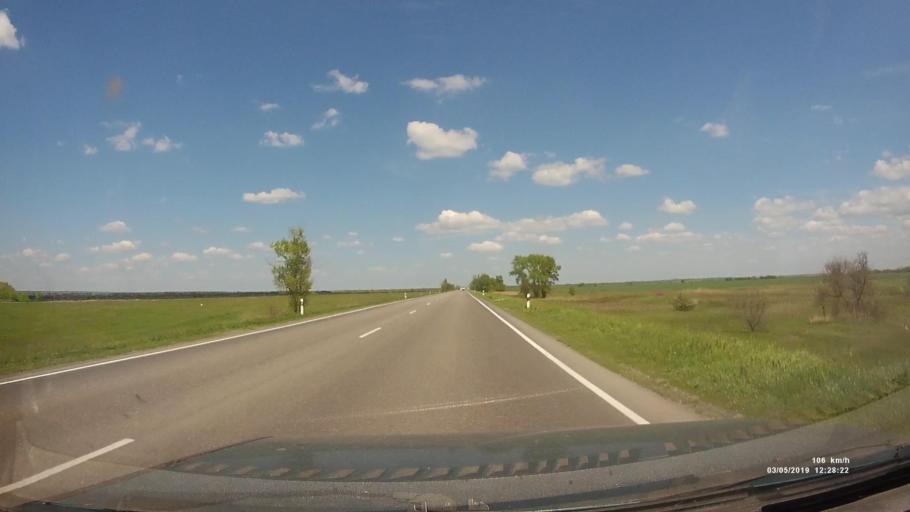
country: RU
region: Rostov
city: Semikarakorsk
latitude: 47.4724
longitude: 40.7280
